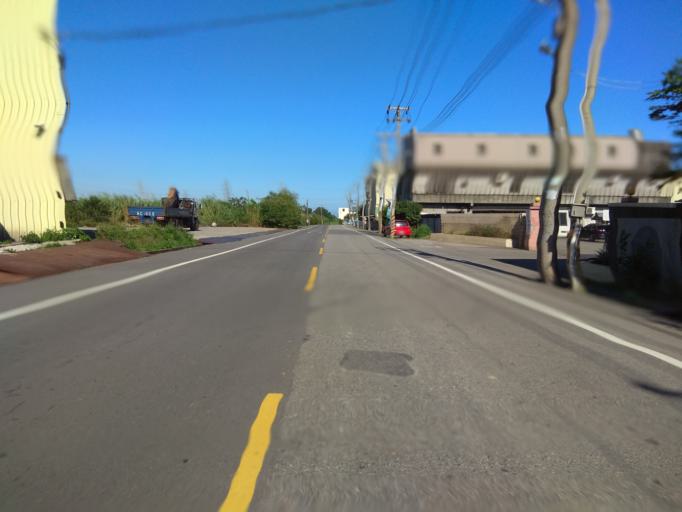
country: TW
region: Taiwan
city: Taoyuan City
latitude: 24.9825
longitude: 121.1355
